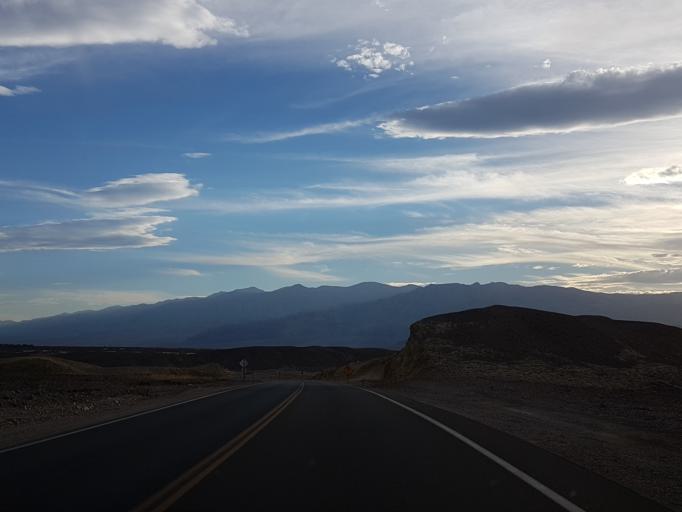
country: US
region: Nevada
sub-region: Nye County
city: Beatty
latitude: 36.4851
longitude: -116.8699
